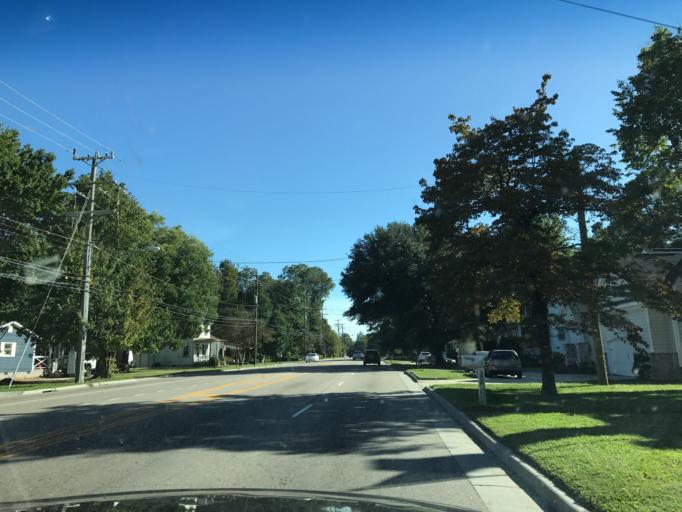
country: US
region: Virginia
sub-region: City of Portsmouth
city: Portsmouth Heights
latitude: 36.7503
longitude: -76.3460
